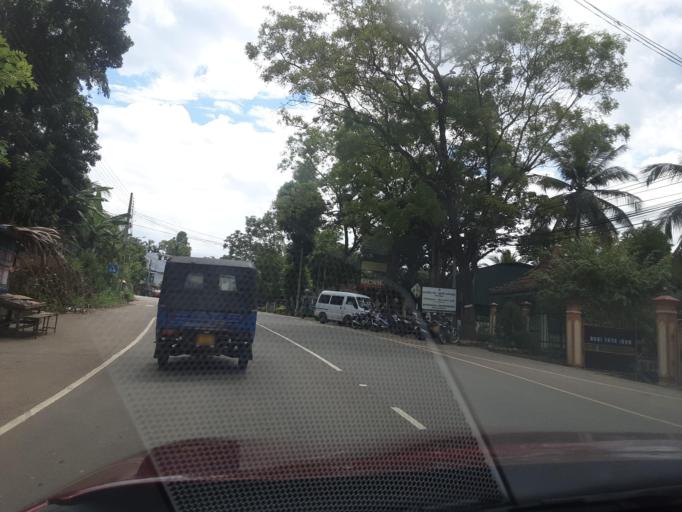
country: LK
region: Uva
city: Monaragala
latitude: 6.8973
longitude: 81.2391
